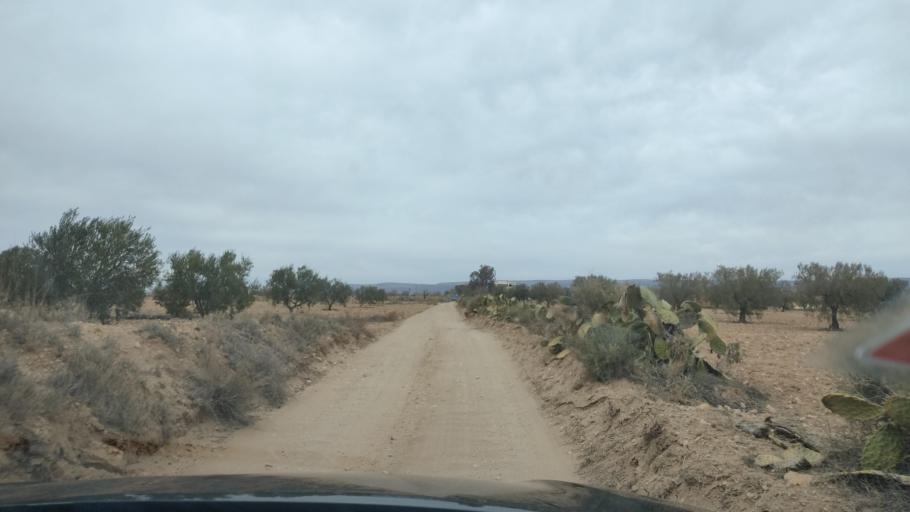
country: TN
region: Al Qasrayn
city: Kasserine
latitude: 35.2254
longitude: 8.9351
